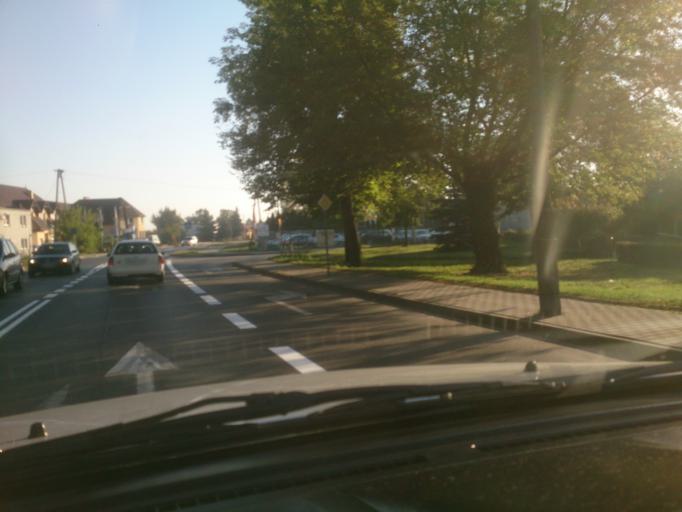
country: PL
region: Kujawsko-Pomorskie
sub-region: Powiat brodnicki
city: Brodnica
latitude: 53.2530
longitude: 19.4191
